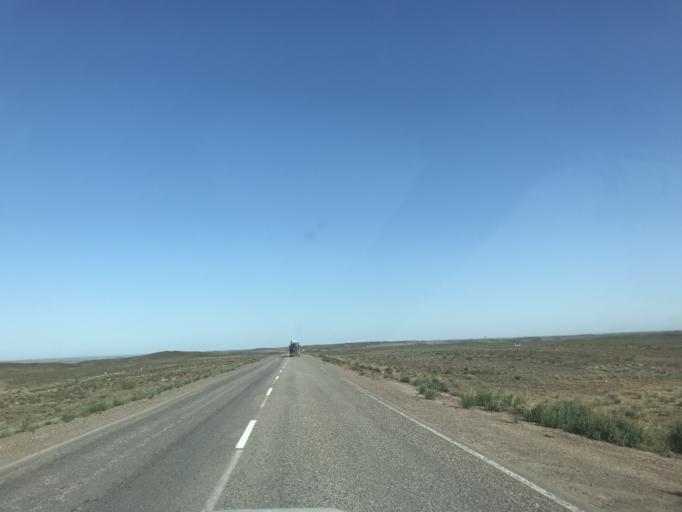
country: KZ
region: Zhambyl
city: Mynaral
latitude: 45.4680
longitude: 73.5633
